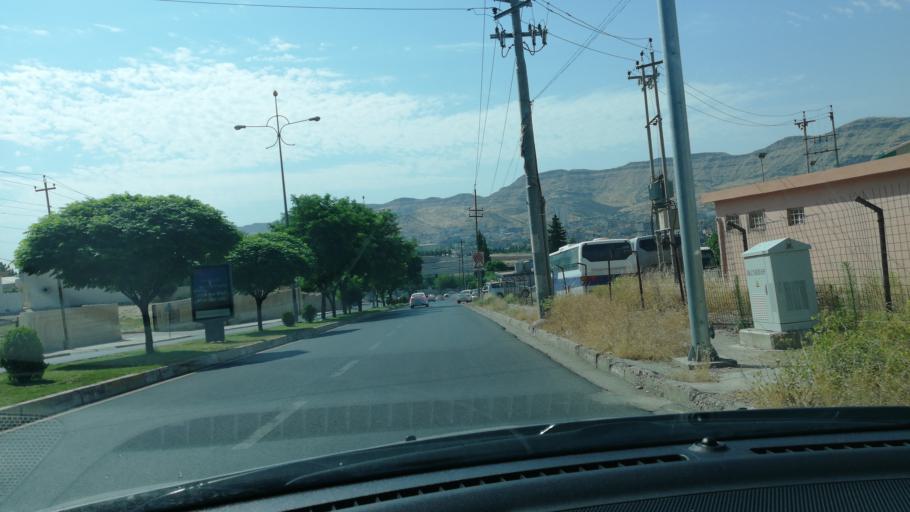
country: IQ
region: Dahuk
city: Dihok
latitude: 36.8622
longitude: 42.9836
